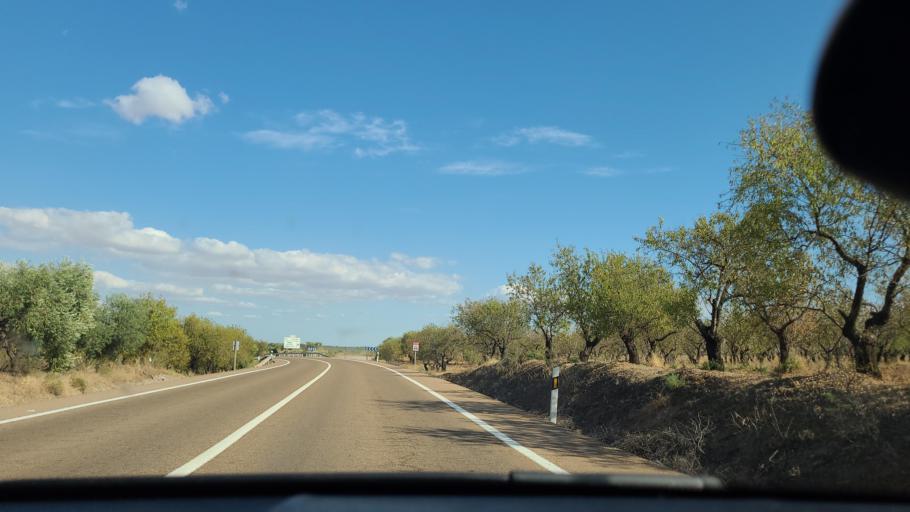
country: ES
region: Extremadura
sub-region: Provincia de Badajoz
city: Usagre
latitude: 38.3456
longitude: -6.1835
